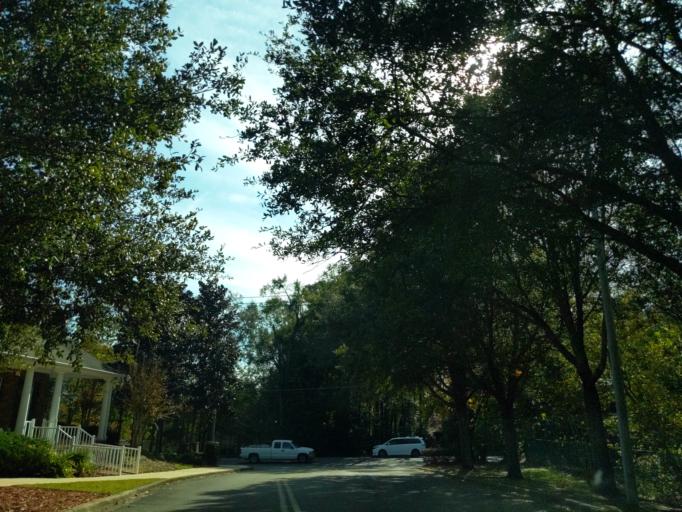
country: US
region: Florida
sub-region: Leon County
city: Tallahassee
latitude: 30.4658
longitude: -84.3405
